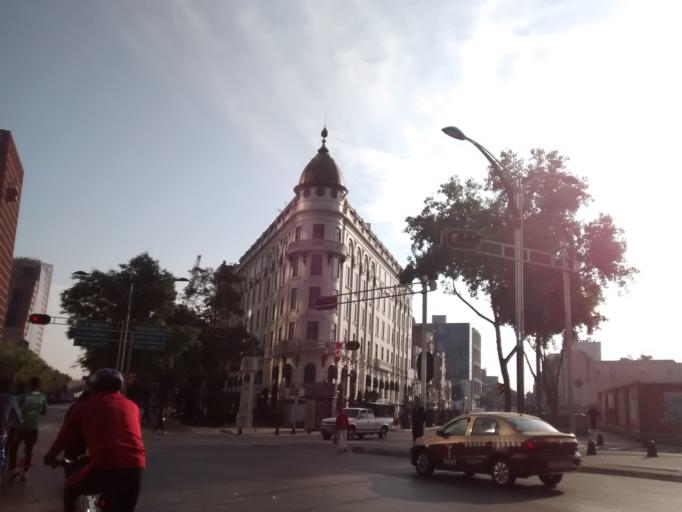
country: MX
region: Mexico City
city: Cuauhtemoc
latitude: 19.4331
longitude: -99.1545
